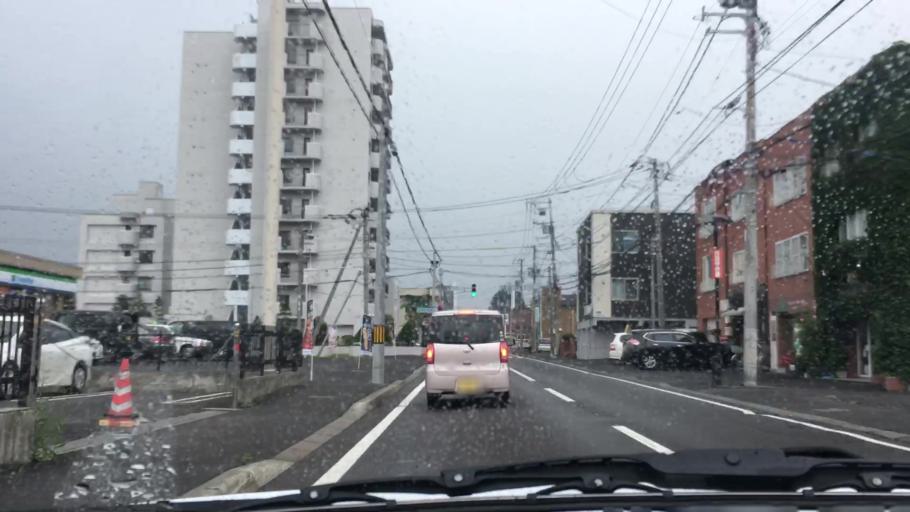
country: JP
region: Hokkaido
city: Sapporo
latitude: 42.9951
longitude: 141.3314
